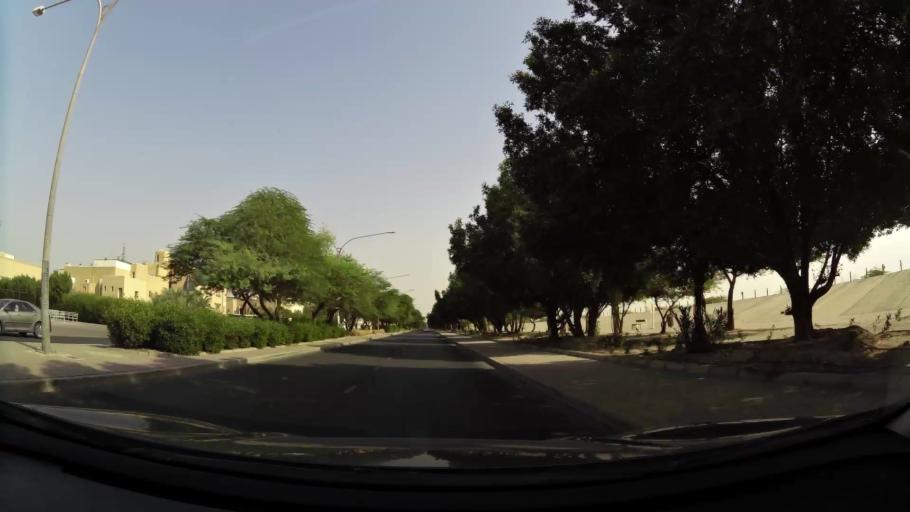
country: KW
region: Muhafazat al Jahra'
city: Al Jahra'
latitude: 29.3199
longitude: 47.6658
